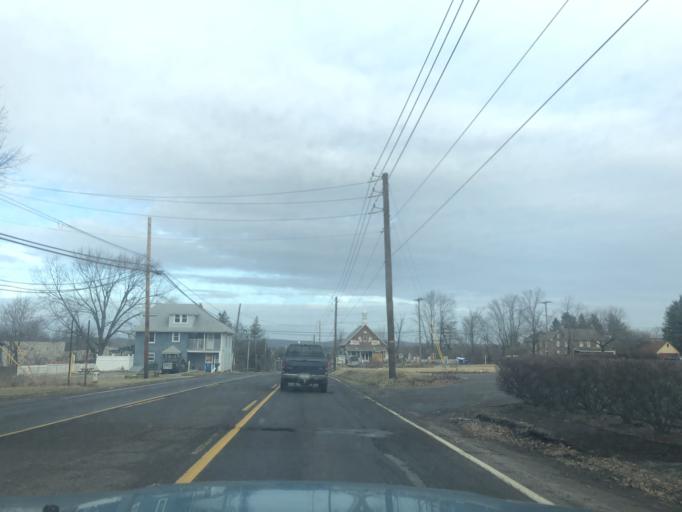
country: US
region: Pennsylvania
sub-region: Montgomery County
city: Telford
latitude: 40.3274
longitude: -75.3030
